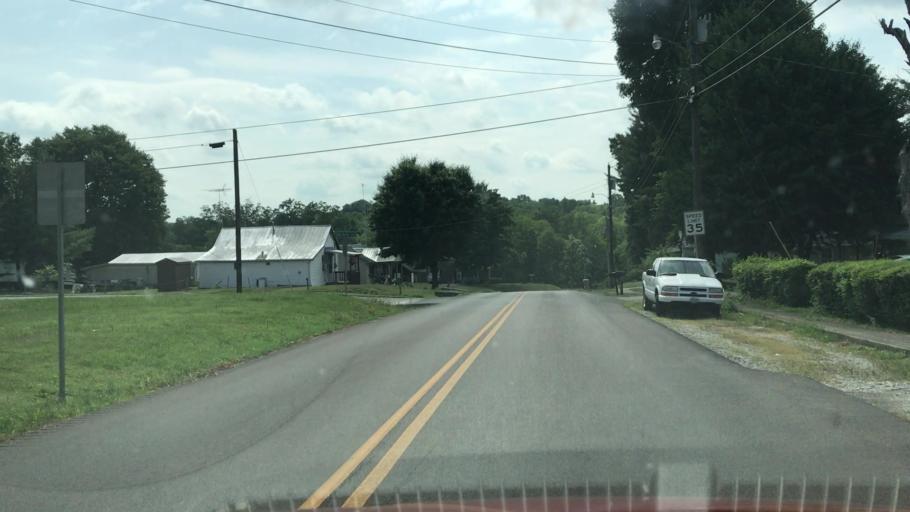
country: US
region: Kentucky
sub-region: Barren County
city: Glasgow
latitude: 36.9895
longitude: -85.9093
